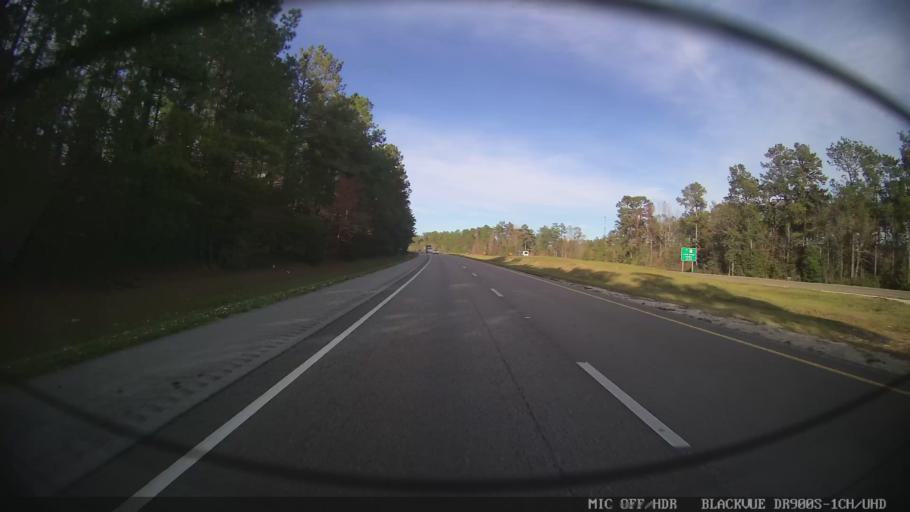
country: US
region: Mississippi
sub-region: Lamar County
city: West Hattiesburg
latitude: 31.2263
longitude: -89.3241
